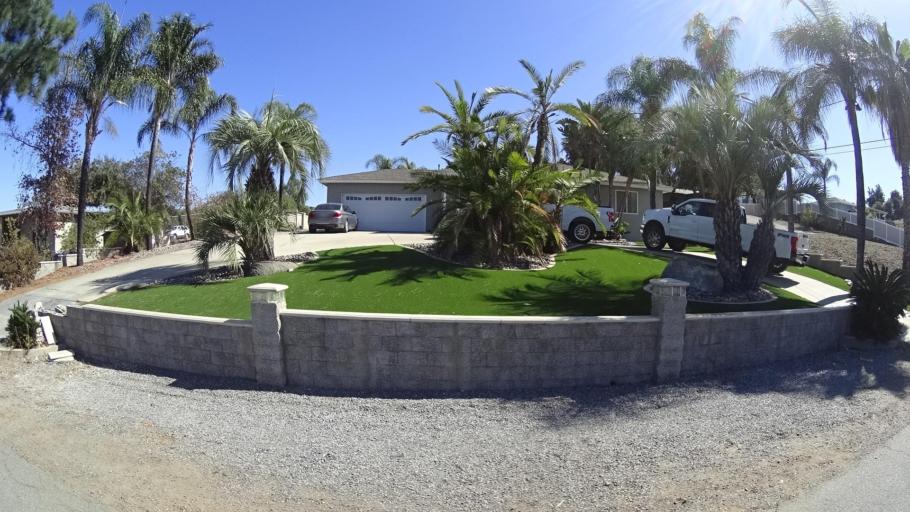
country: US
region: California
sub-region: San Diego County
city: Bostonia
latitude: 32.8179
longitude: -116.9303
